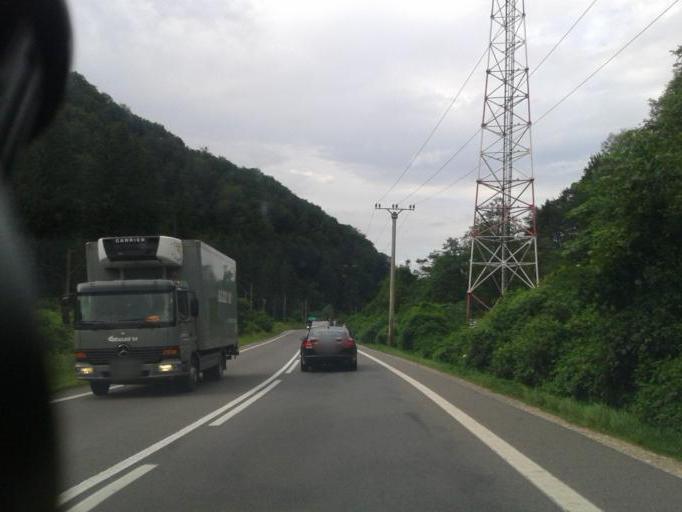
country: RO
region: Brasov
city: Brasov
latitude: 45.5750
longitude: 25.6154
